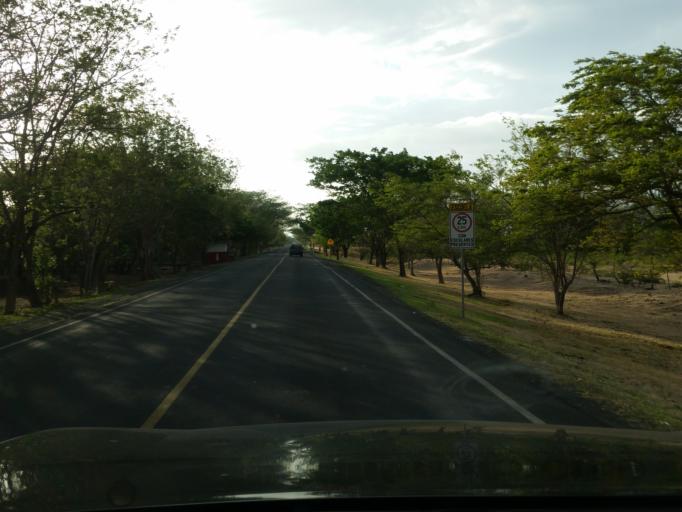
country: NI
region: Rivas
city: Belen
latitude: 11.6066
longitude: -85.9370
